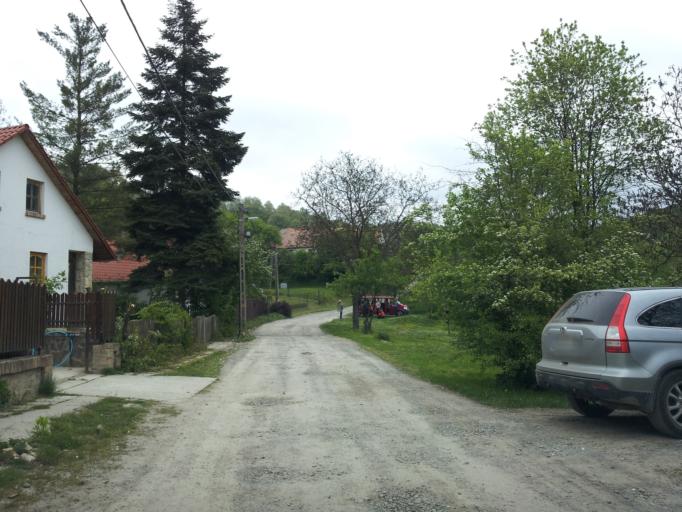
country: HU
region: Baranya
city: Hosszuheteny
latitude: 46.1875
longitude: 18.3589
